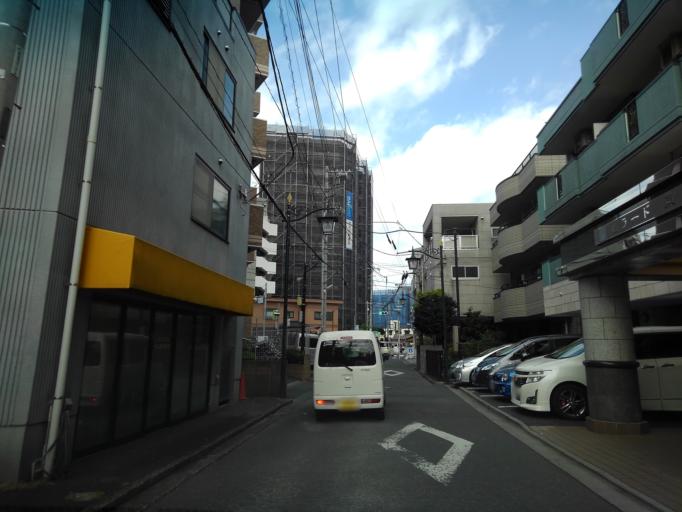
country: JP
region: Tokyo
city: Higashimurayama-shi
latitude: 35.7610
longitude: 139.4678
